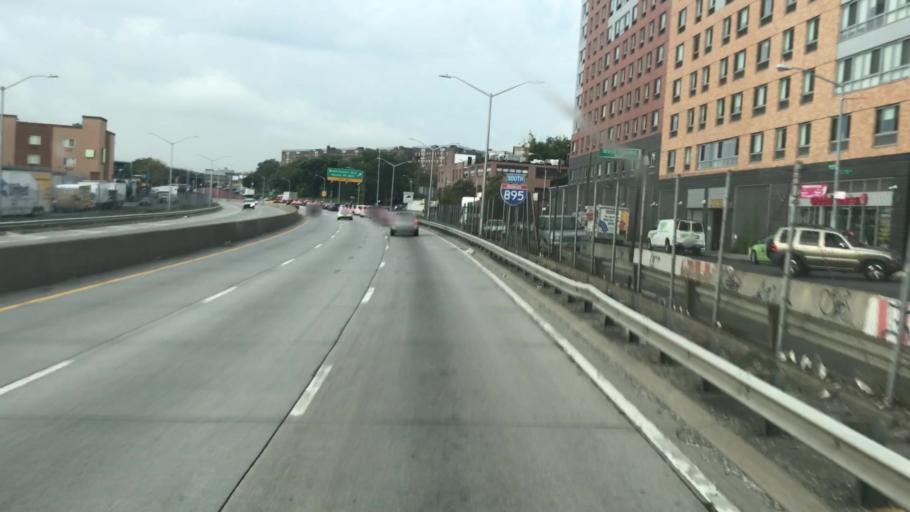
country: US
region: New York
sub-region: Bronx
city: The Bronx
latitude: 40.8325
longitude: -73.8845
